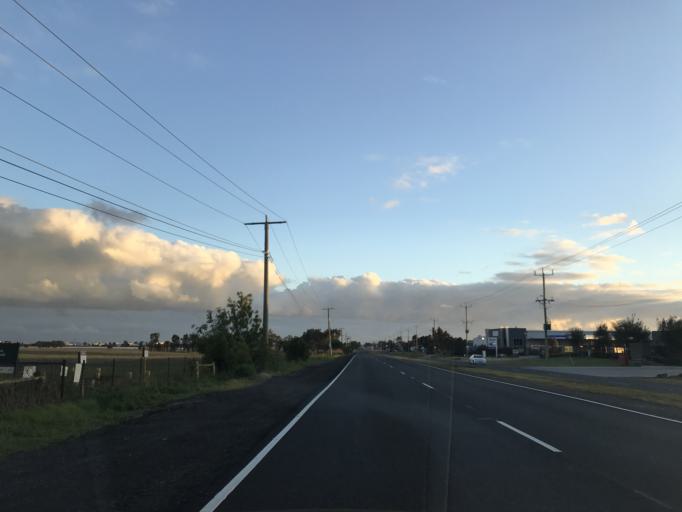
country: AU
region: Victoria
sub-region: Brimbank
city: Derrimut
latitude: -37.8009
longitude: 144.7891
